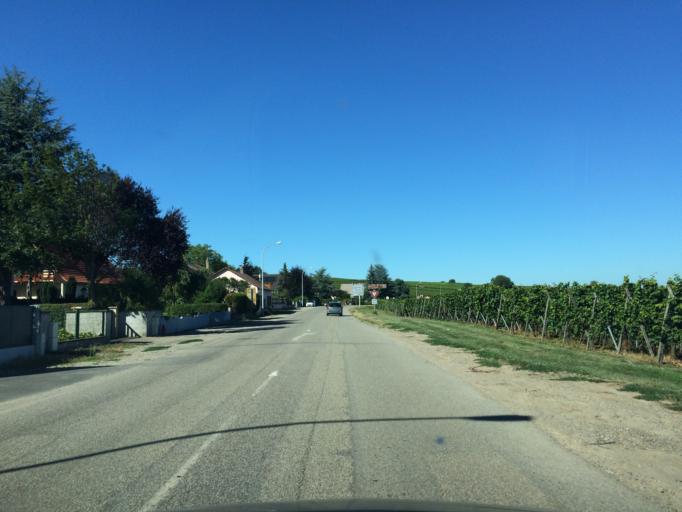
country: FR
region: Alsace
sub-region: Departement du Haut-Rhin
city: Herrlisheim-pres-Colmar
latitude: 48.0148
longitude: 7.3077
